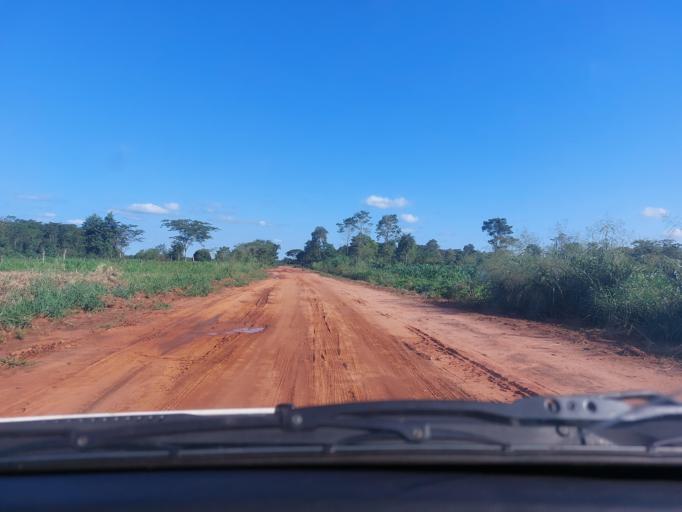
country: PY
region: San Pedro
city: Guayaybi
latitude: -24.5281
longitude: -56.5455
